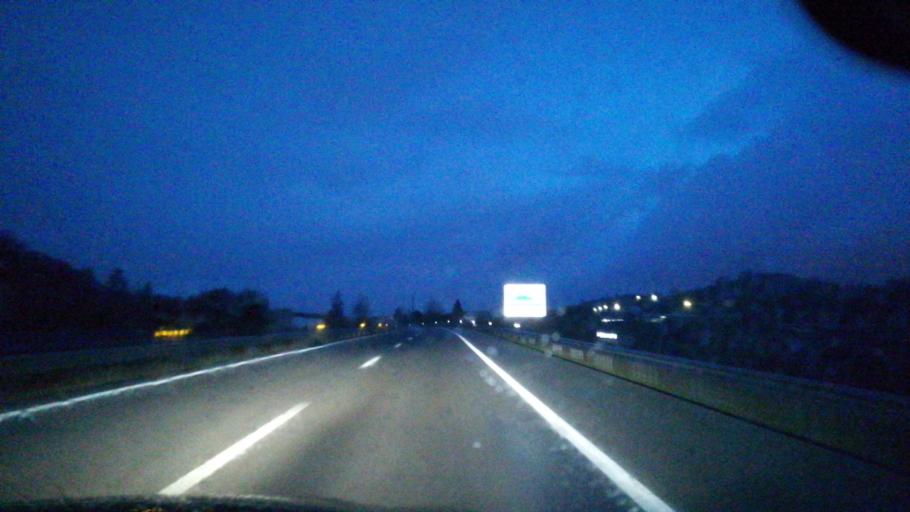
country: PT
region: Braga
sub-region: Guimaraes
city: Candoso
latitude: 41.4144
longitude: -8.3245
